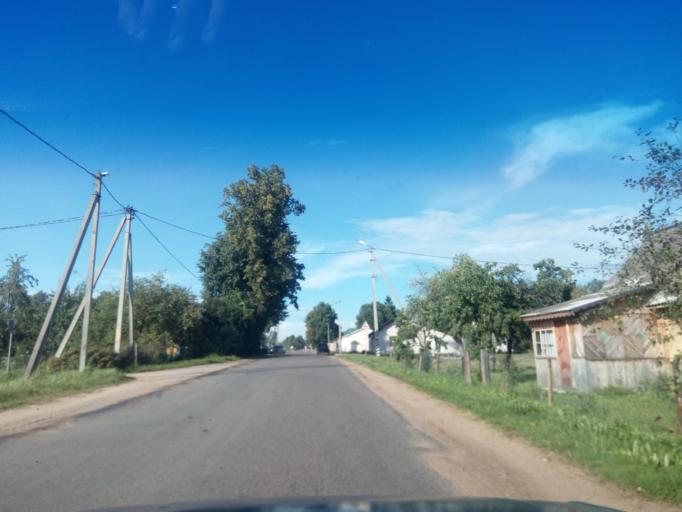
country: BY
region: Vitebsk
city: Dzisna
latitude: 55.6672
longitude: 28.3276
